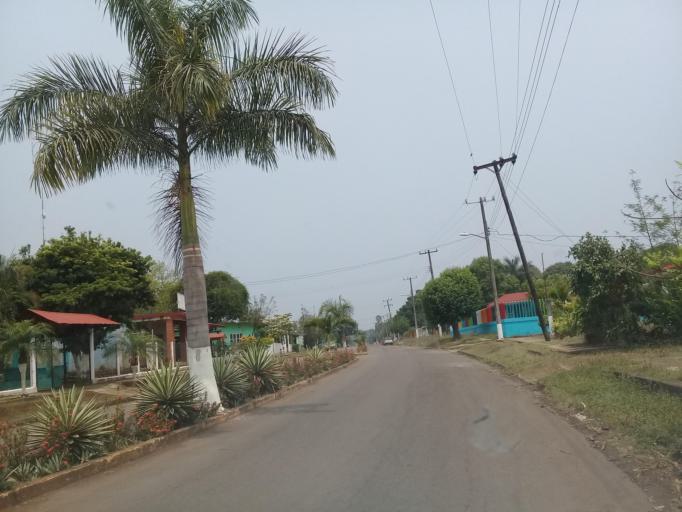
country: MX
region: Veracruz
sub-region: Tezonapa
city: Laguna Chica (Pueblo Nuevo)
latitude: 18.5154
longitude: -96.7178
